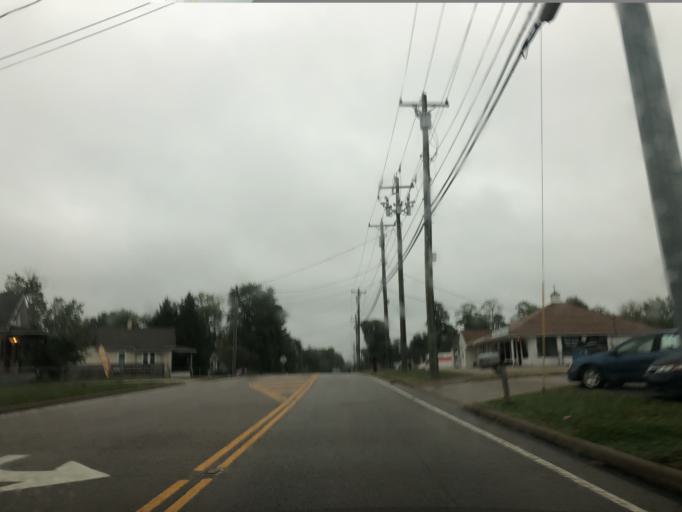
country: US
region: Ohio
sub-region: Clermont County
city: Mulberry
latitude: 39.1926
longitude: -84.2488
